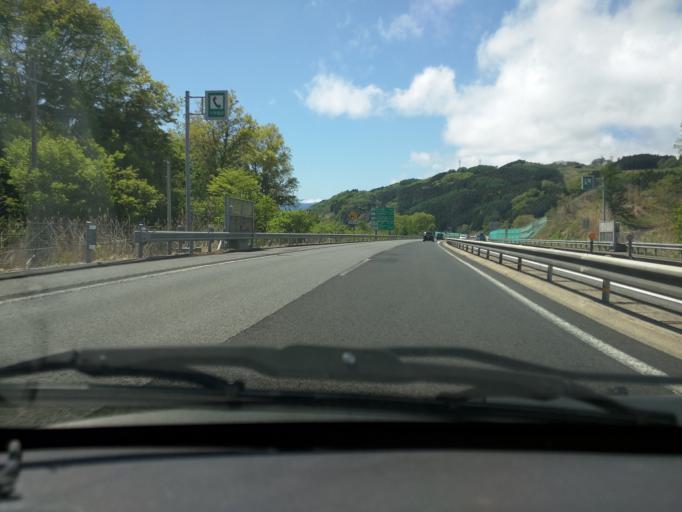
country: JP
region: Nagano
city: Nakano
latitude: 36.7885
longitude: 138.3210
